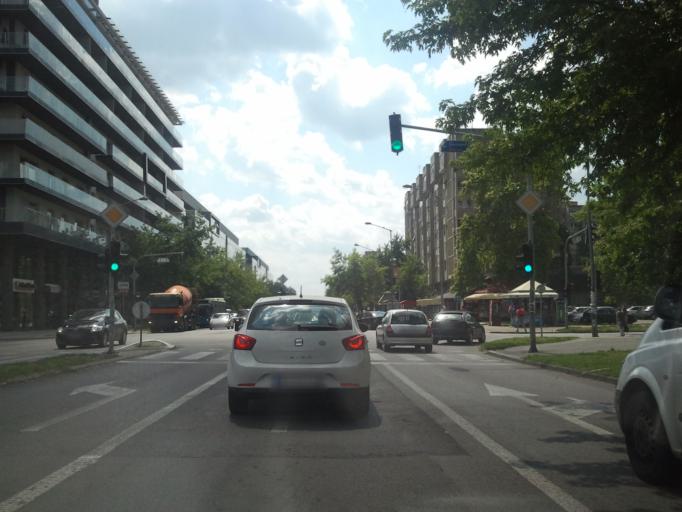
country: RS
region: Autonomna Pokrajina Vojvodina
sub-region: Juznobacki Okrug
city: Novi Sad
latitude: 45.2404
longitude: 19.8383
